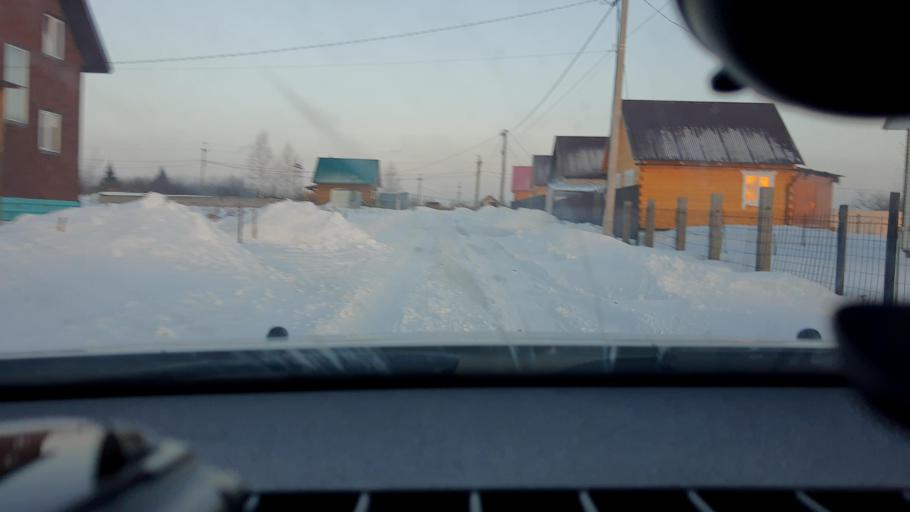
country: RU
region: Bashkortostan
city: Iglino
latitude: 54.8622
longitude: 56.4785
